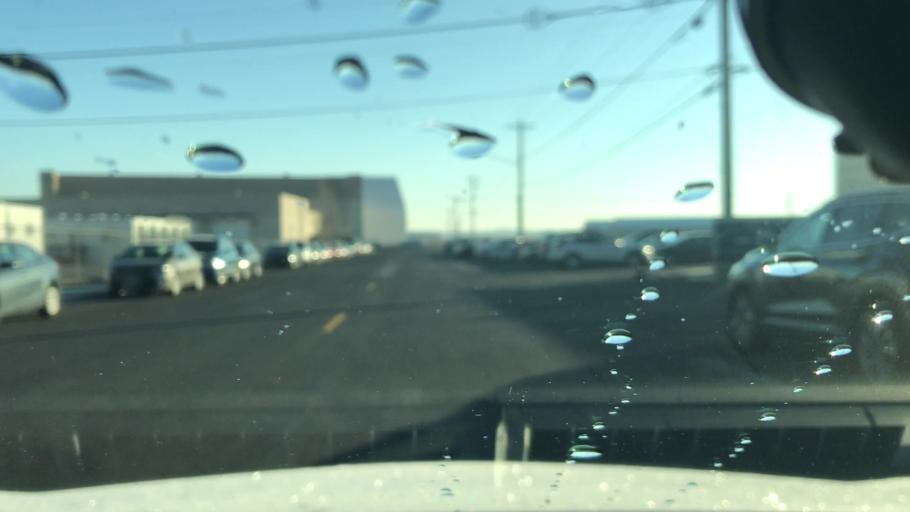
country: US
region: Washington
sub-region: Grant County
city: Moses Lake North
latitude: 47.1883
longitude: -119.3193
